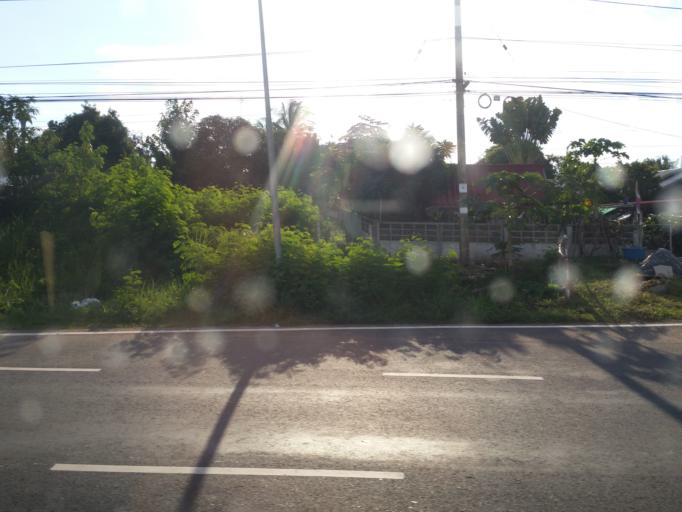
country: TH
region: Changwat Ubon Ratchathani
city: Sirindhorn
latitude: 15.1991
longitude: 105.3698
